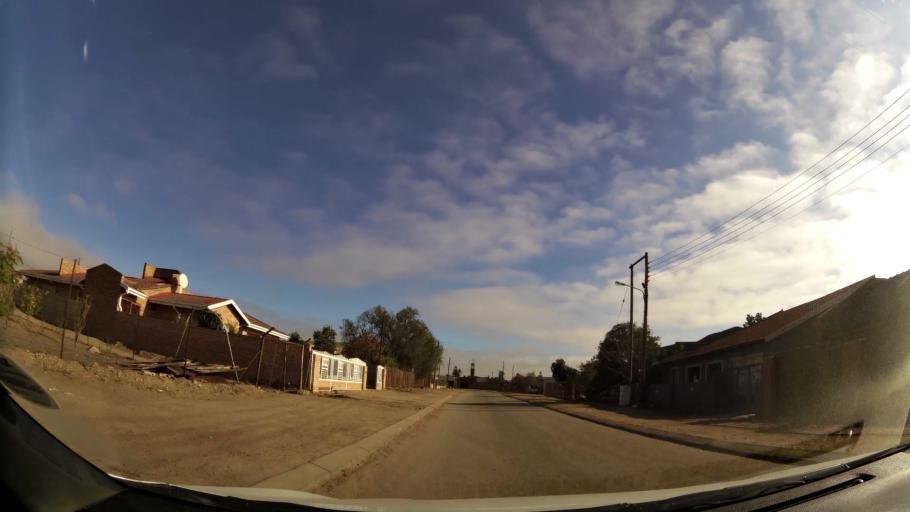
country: ZA
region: Limpopo
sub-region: Capricorn District Municipality
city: Polokwane
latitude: -23.8475
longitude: 29.3867
